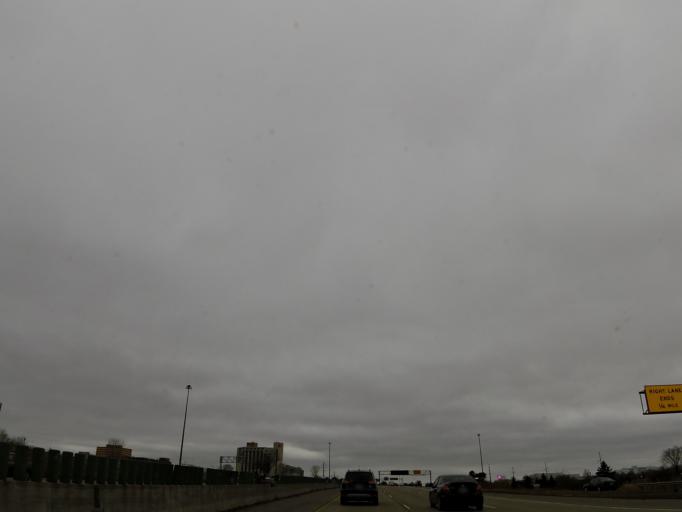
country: US
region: Minnesota
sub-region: Dakota County
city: Eagan
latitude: 44.8627
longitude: -93.2116
